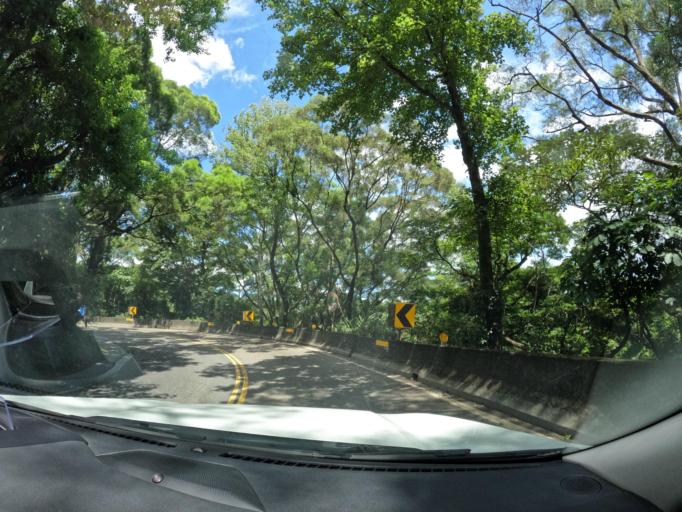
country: TW
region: Taipei
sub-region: Taipei
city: Banqiao
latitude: 25.1148
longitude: 121.3877
